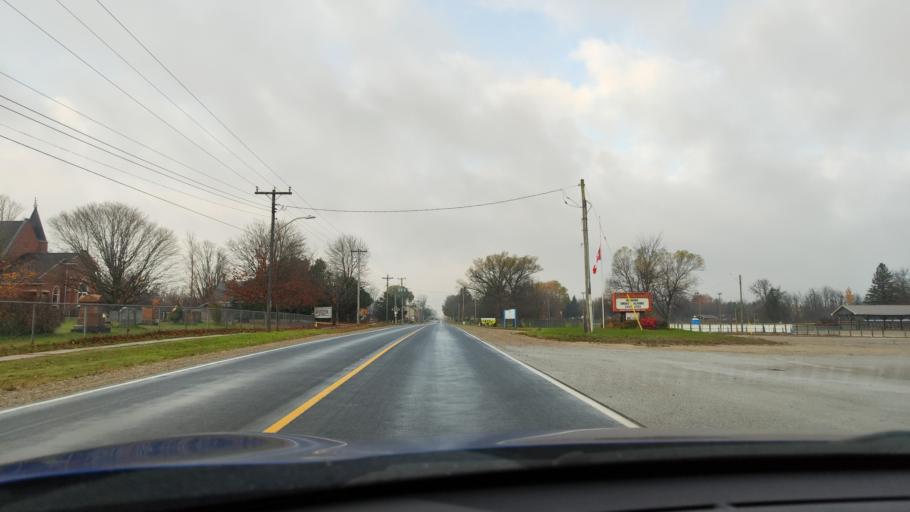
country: CA
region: Ontario
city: Angus
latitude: 44.3592
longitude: -79.9678
